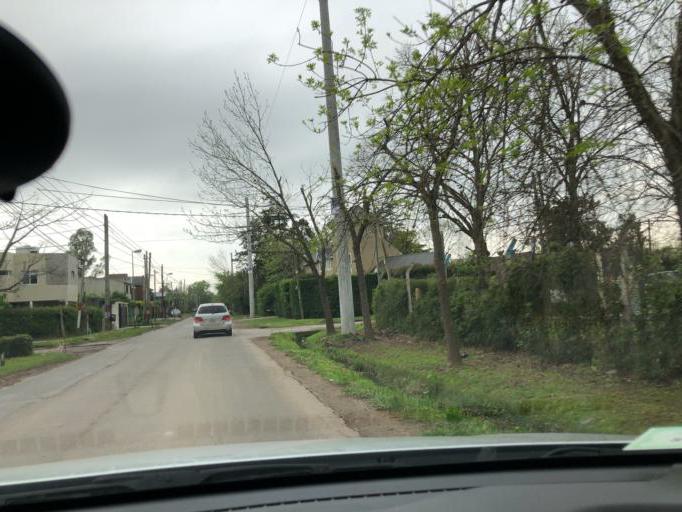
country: AR
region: Buenos Aires
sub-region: Partido de La Plata
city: La Plata
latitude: -34.8907
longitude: -58.0636
